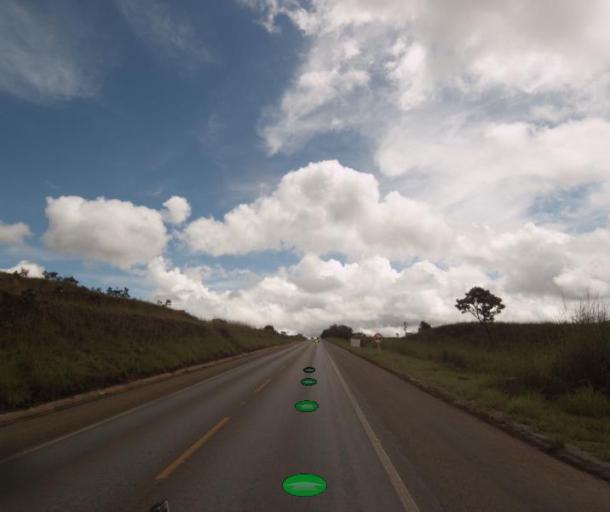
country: BR
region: Federal District
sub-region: Brasilia
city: Brasilia
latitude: -15.7439
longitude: -48.3603
